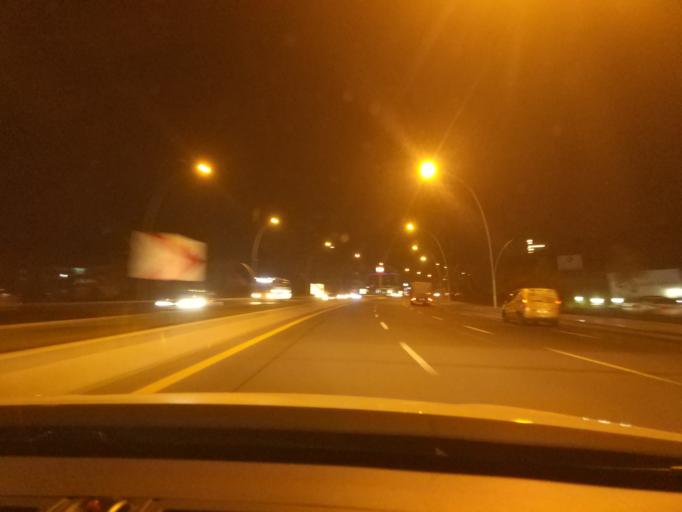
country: TR
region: Ankara
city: Mamak
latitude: 40.0662
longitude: 32.9229
